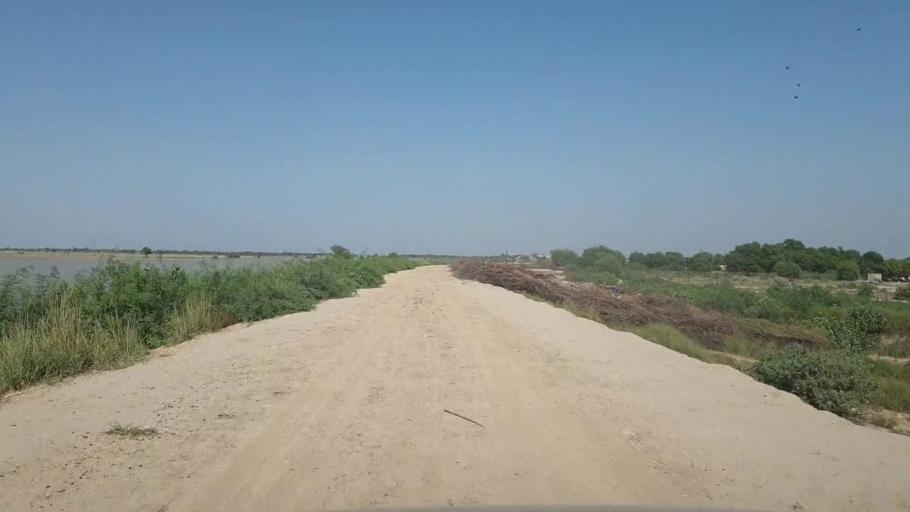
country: PK
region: Sindh
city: Matiari
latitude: 25.6393
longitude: 68.4870
